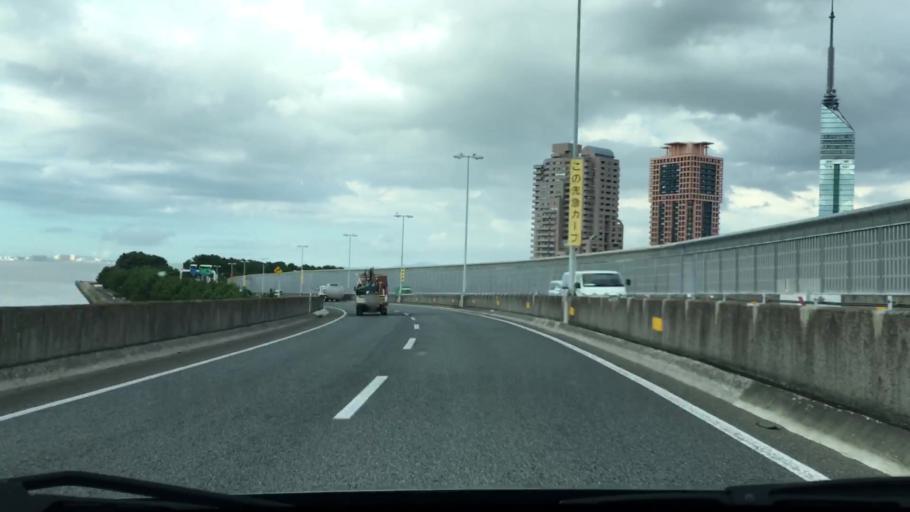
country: JP
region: Fukuoka
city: Fukuoka-shi
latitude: 33.5896
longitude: 130.3448
